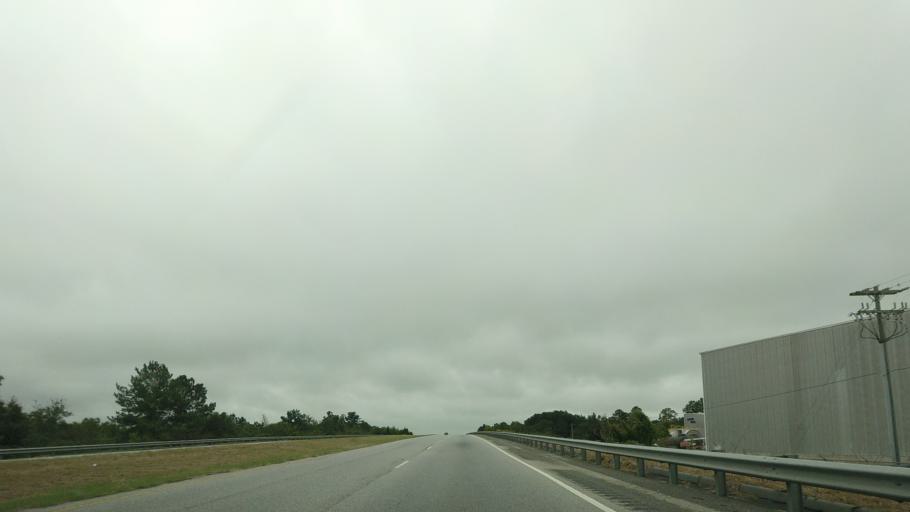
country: US
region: Georgia
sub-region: Lowndes County
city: Valdosta
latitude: 30.8327
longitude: -83.2282
